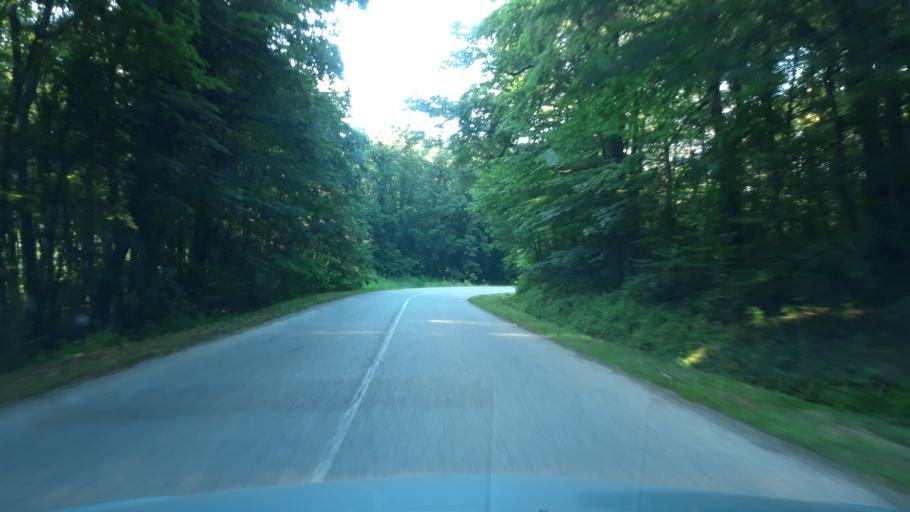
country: RS
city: Glozan
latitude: 45.1529
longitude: 19.5795
